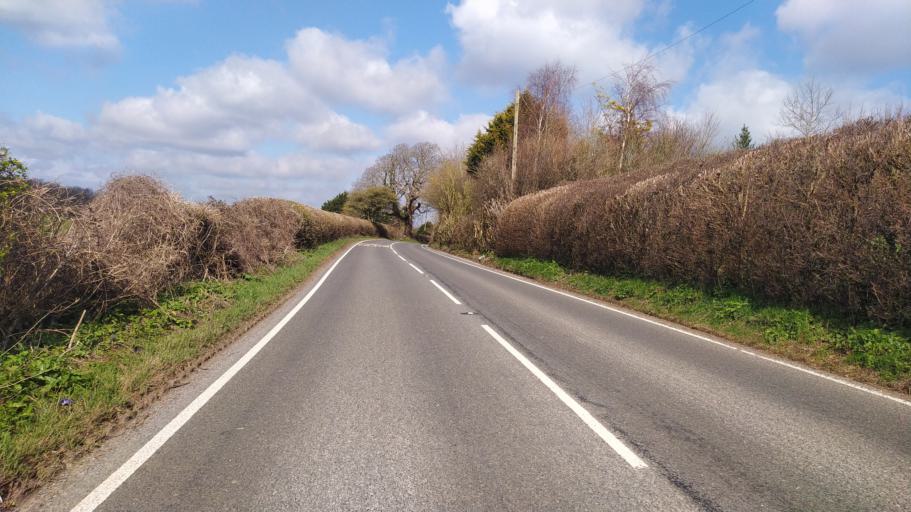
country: GB
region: England
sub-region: Dorset
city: Beaminster
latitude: 50.7727
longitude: -2.7324
